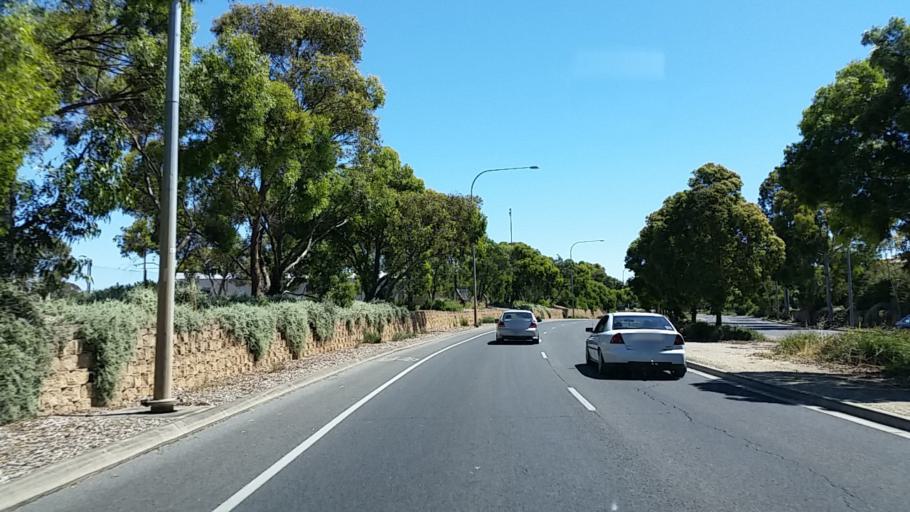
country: AU
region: South Australia
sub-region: City of West Torrens
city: Thebarton
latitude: -34.9274
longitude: 138.5789
